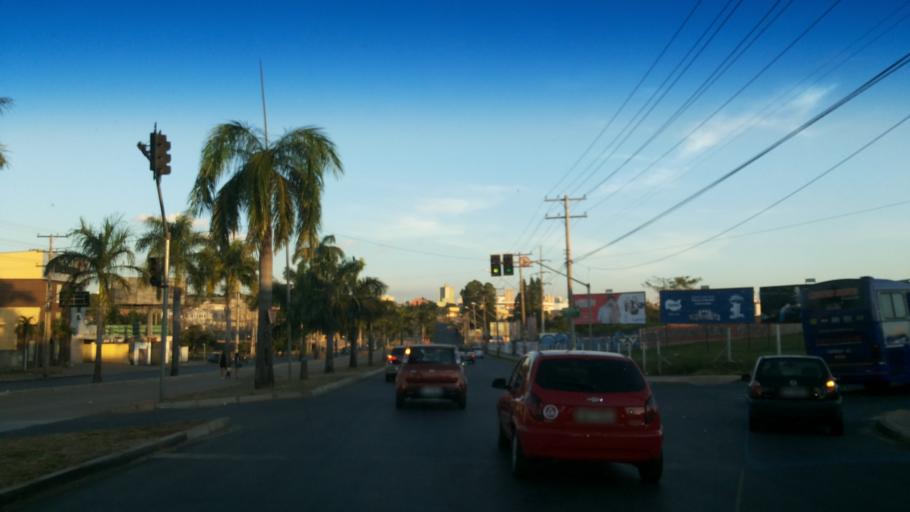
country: BR
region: Goias
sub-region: Goiania
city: Goiania
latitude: -16.6528
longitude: -49.2637
